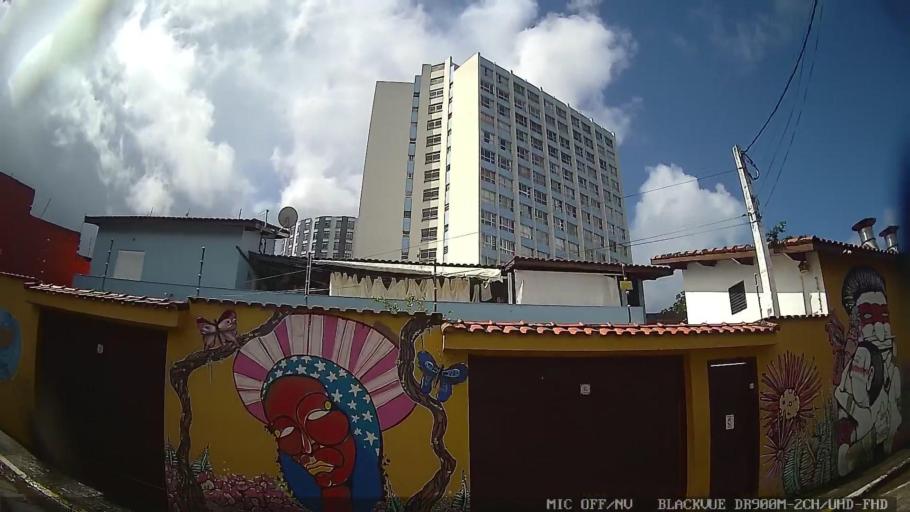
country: BR
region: Sao Paulo
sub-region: Itanhaem
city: Itanhaem
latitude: -24.1902
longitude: -46.8022
